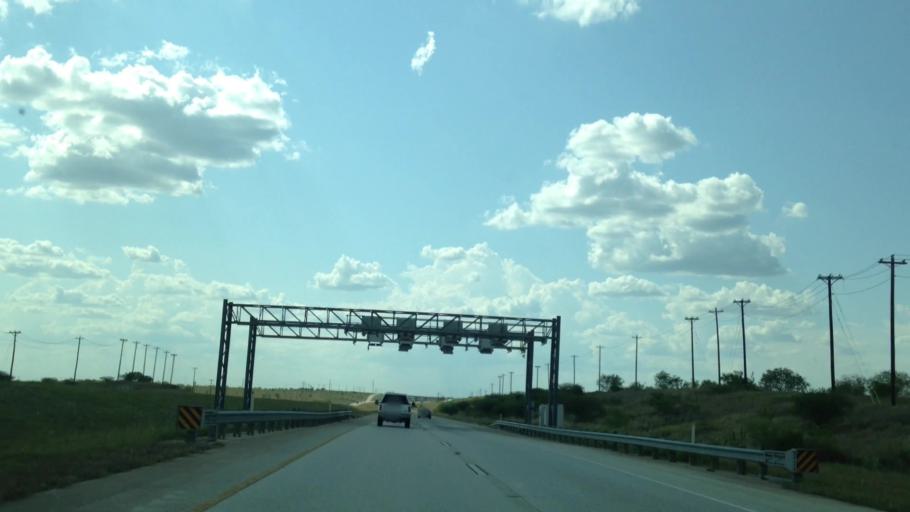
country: US
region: Texas
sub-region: Travis County
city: Onion Creek
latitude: 30.0950
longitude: -97.7627
